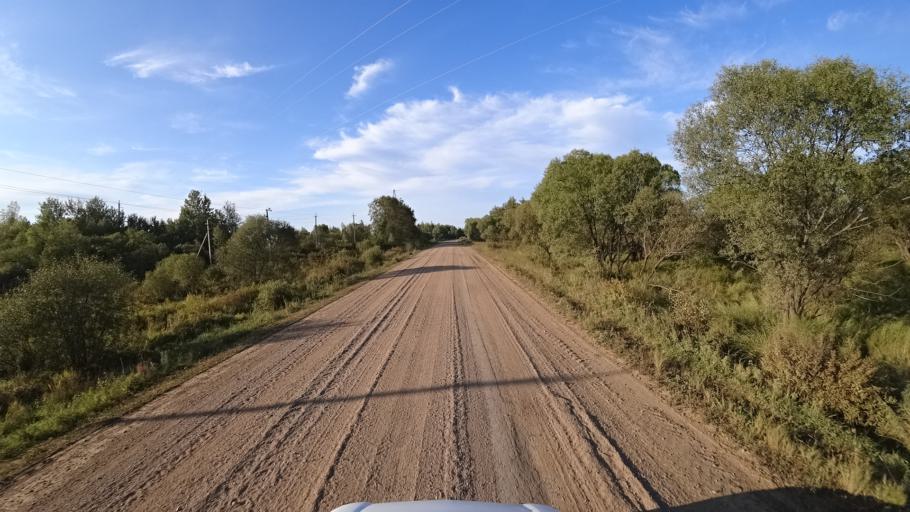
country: RU
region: Amur
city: Arkhara
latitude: 49.3656
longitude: 130.1362
